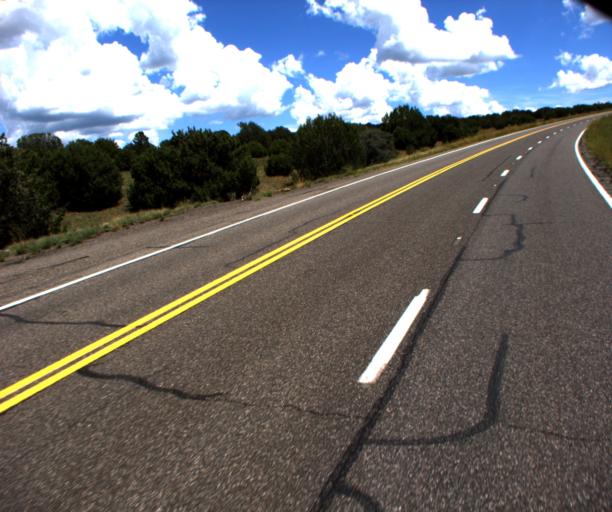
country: US
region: Arizona
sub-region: Yavapai County
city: Lake Montezuma
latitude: 34.4933
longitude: -111.6292
